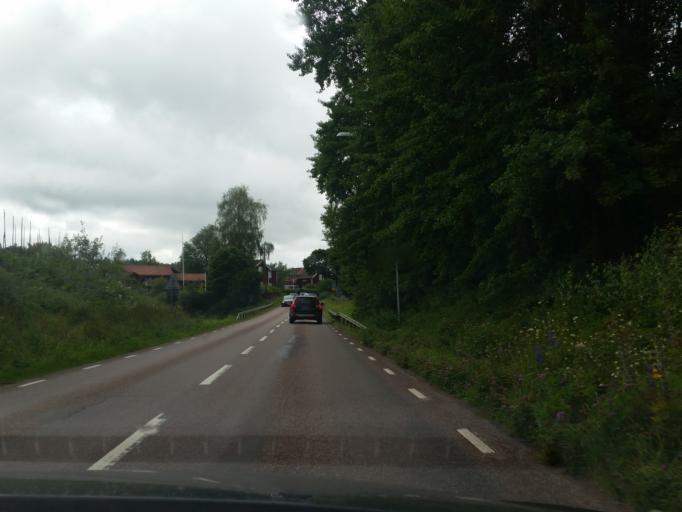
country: SE
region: Dalarna
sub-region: Leksand Municipality
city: Leksand
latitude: 60.7251
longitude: 14.9561
